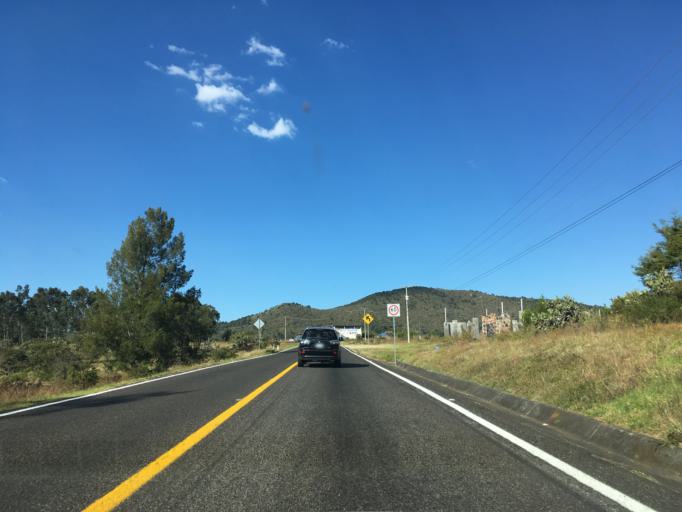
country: MX
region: Michoacan
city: Tzintzuntzan
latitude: 19.5776
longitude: -101.5769
